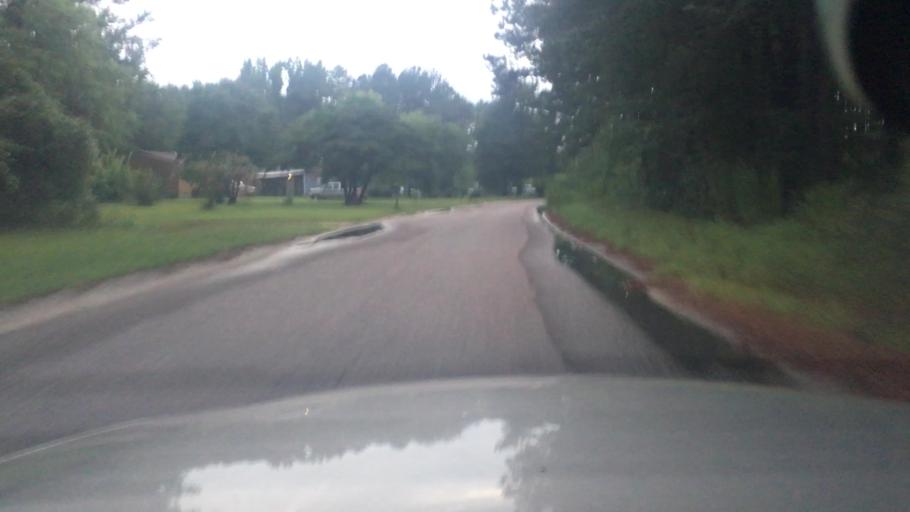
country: US
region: North Carolina
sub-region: Cumberland County
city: Hope Mills
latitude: 34.9623
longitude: -78.9357
